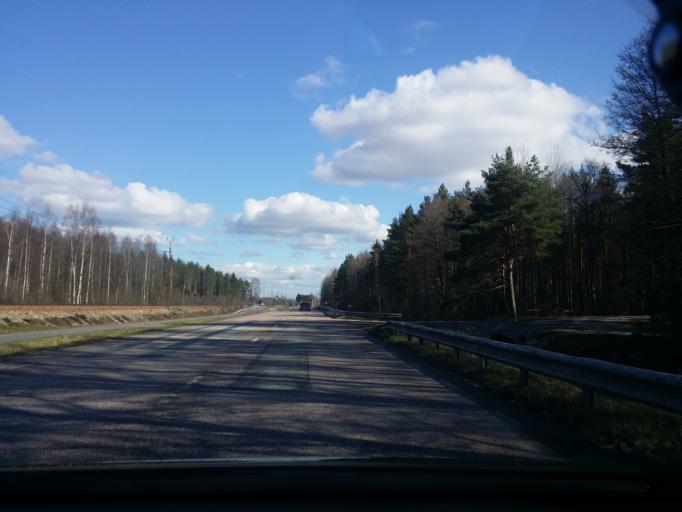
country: SE
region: Vaestmanland
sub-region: Sala Kommun
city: Sala
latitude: 59.9388
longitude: 16.5609
